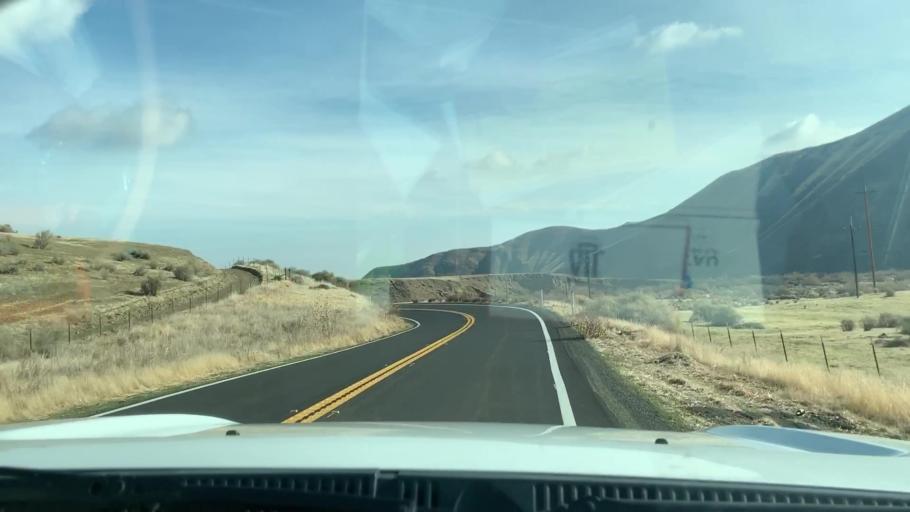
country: US
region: California
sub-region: Fresno County
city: Coalinga
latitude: 36.0998
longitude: -120.4181
